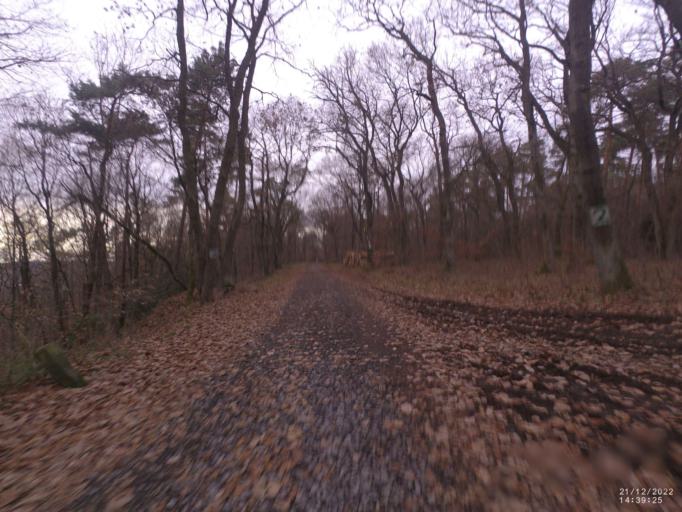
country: DE
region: Rheinland-Pfalz
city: Sinzig
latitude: 50.5275
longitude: 7.2613
